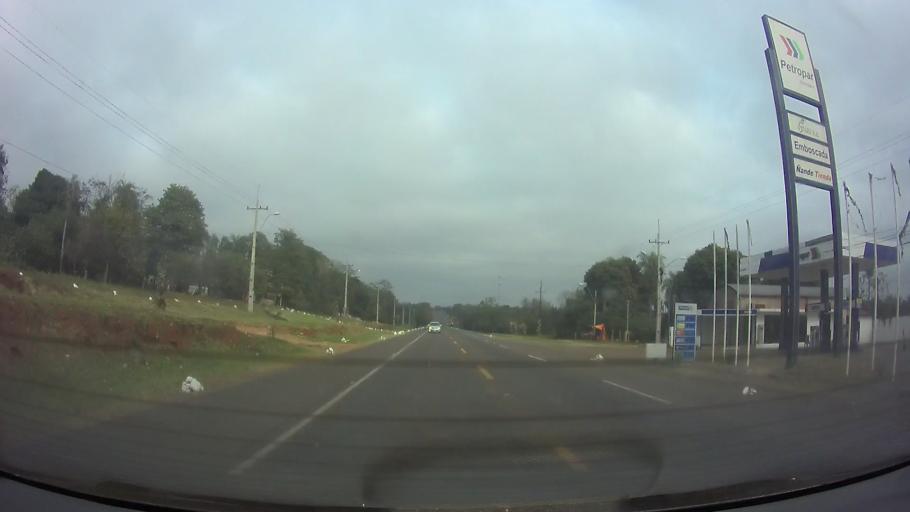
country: PY
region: Cordillera
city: Emboscada
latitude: -25.1208
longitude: -57.3308
